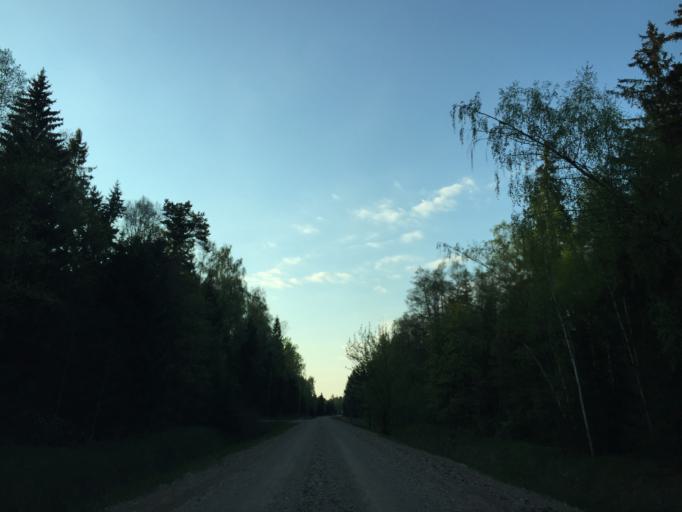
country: LV
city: Tireli
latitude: 56.8459
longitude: 23.6966
